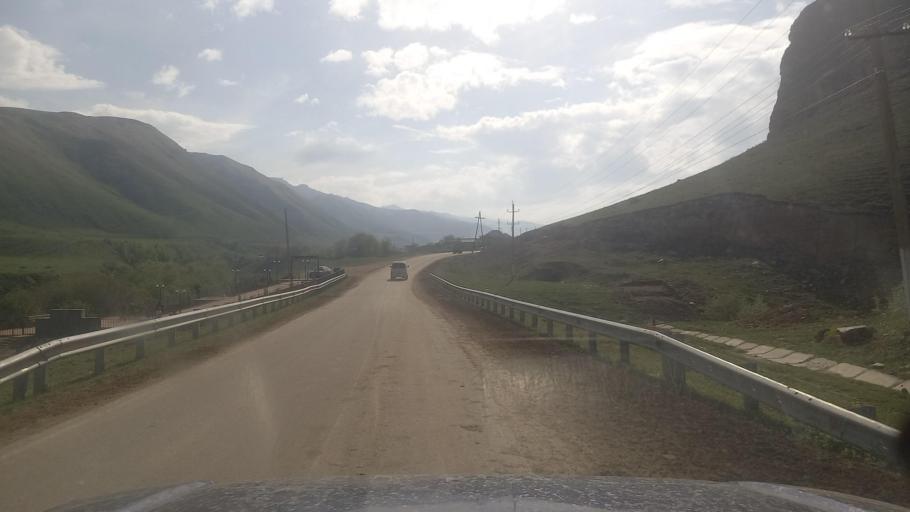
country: RU
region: Kabardino-Balkariya
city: Kamennomostskoye
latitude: 43.7336
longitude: 42.9633
